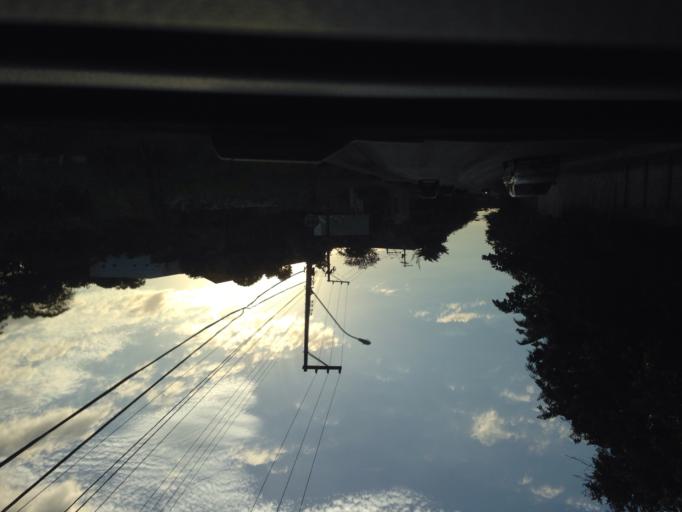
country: BR
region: Espirito Santo
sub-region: Guarapari
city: Guarapari
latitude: -20.6277
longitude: -40.4753
